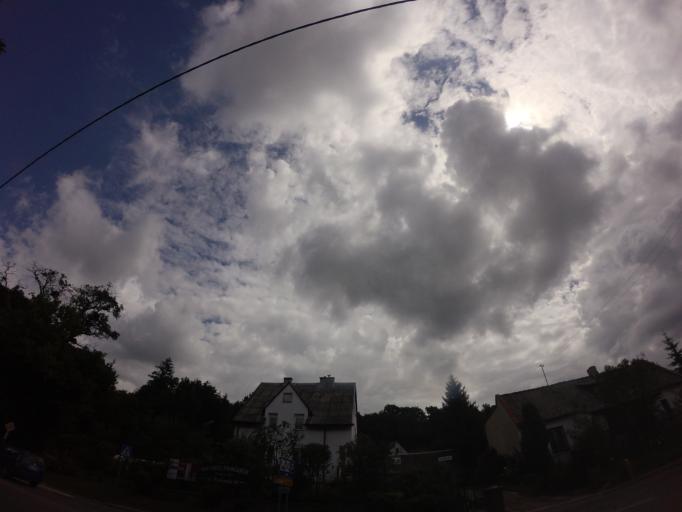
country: PL
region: Lublin Voivodeship
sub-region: Powiat pulawski
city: Kazimierz Dolny
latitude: 51.3092
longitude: 21.9494
